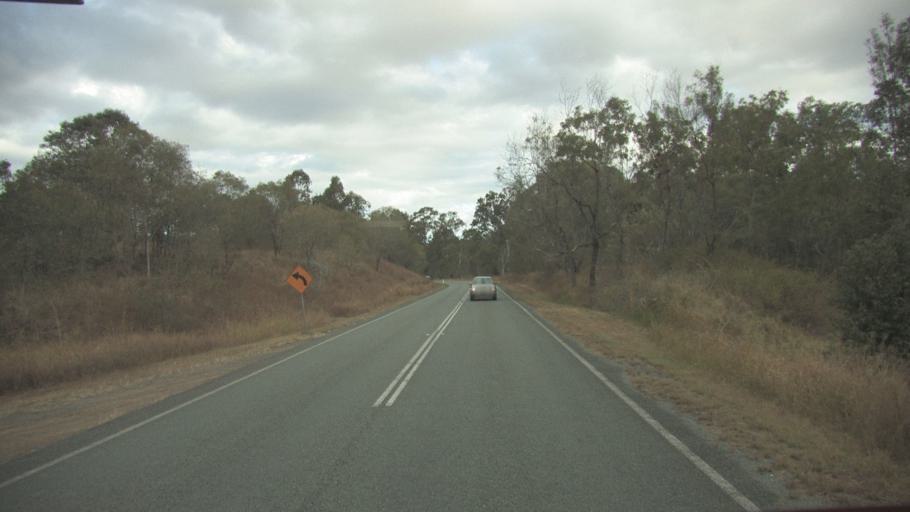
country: AU
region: Queensland
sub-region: Logan
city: Cedar Vale
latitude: -27.8955
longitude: 153.0880
